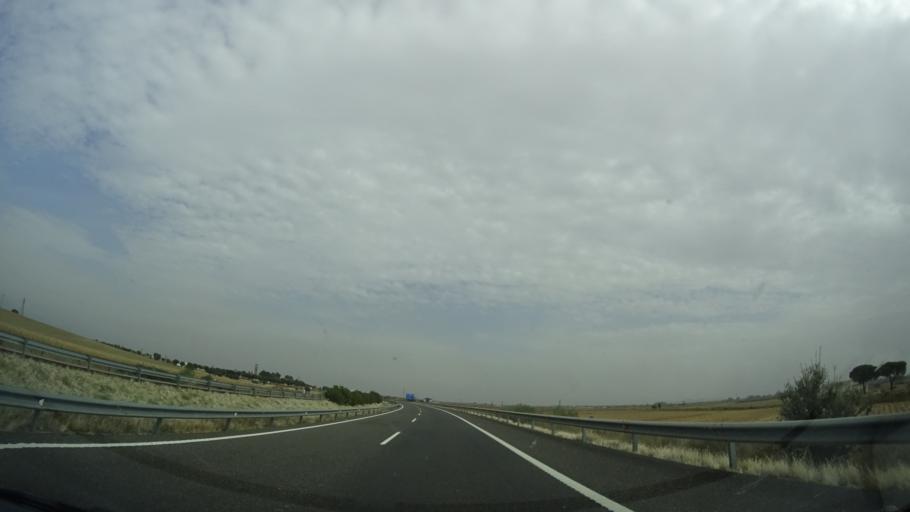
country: ES
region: Extremadura
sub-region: Provincia de Badajoz
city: Santa Amalia
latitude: 39.0679
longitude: -6.0439
